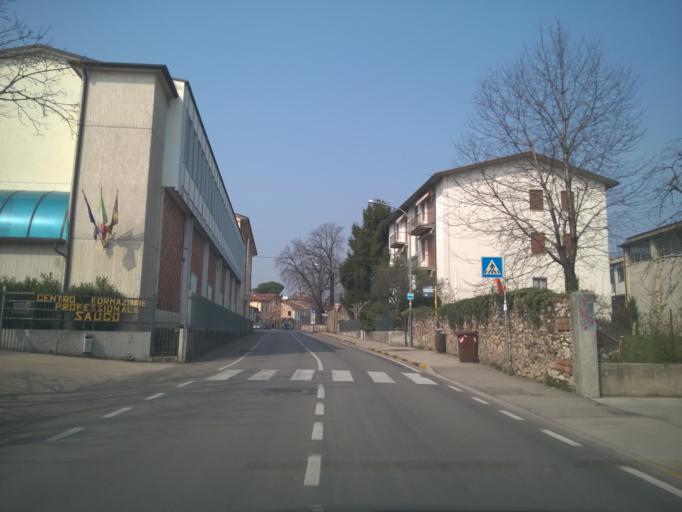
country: IT
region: Veneto
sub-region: Provincia di Vicenza
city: Thiene
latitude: 45.7026
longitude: 11.4855
